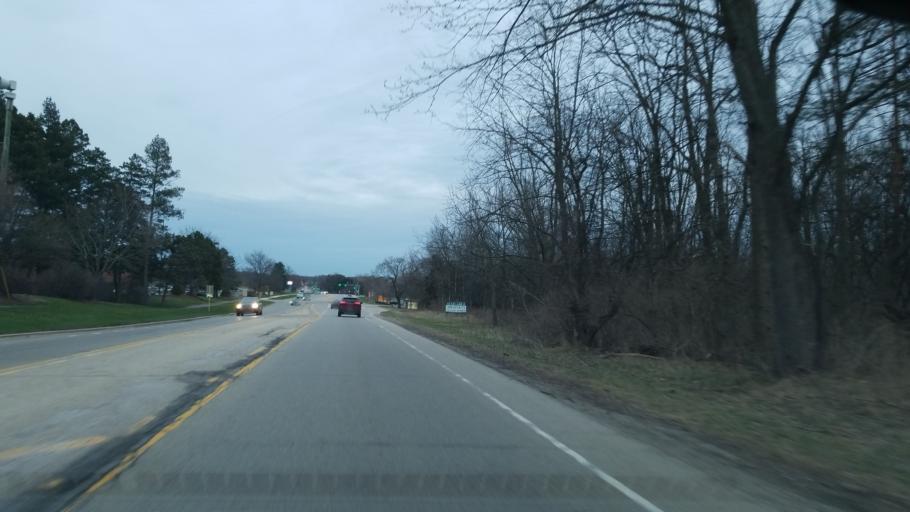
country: US
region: Illinois
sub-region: Kane County
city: Sleepy Hollow
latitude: 42.1000
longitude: -88.3020
